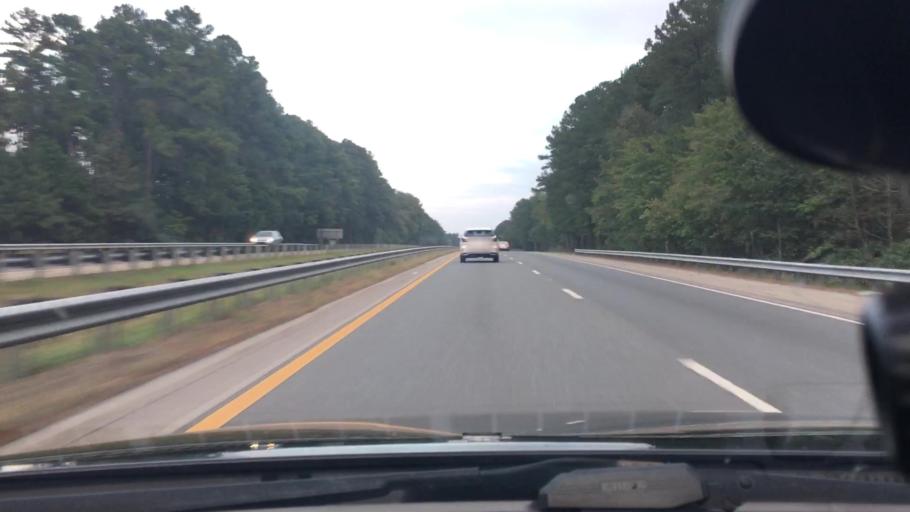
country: US
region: North Carolina
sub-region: Chatham County
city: Pittsboro
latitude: 35.6294
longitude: -79.0714
